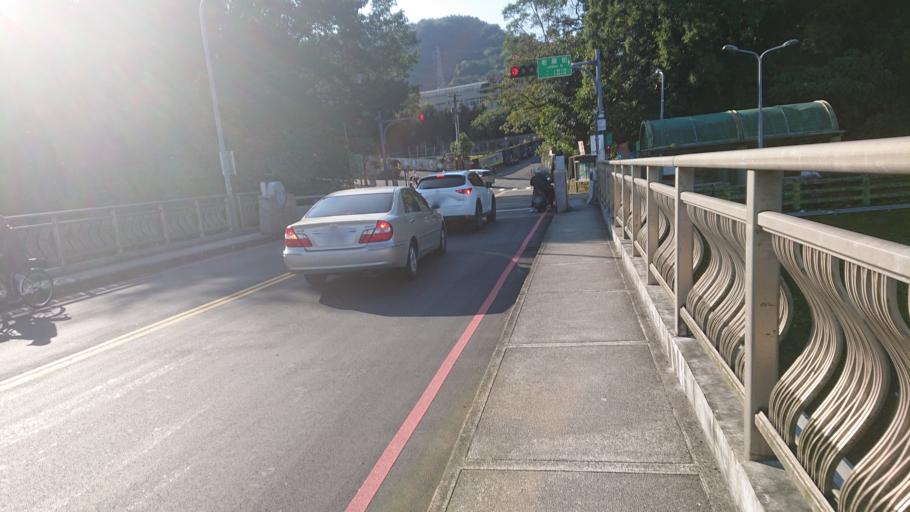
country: TW
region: Taipei
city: Taipei
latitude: 24.9802
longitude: 121.5676
